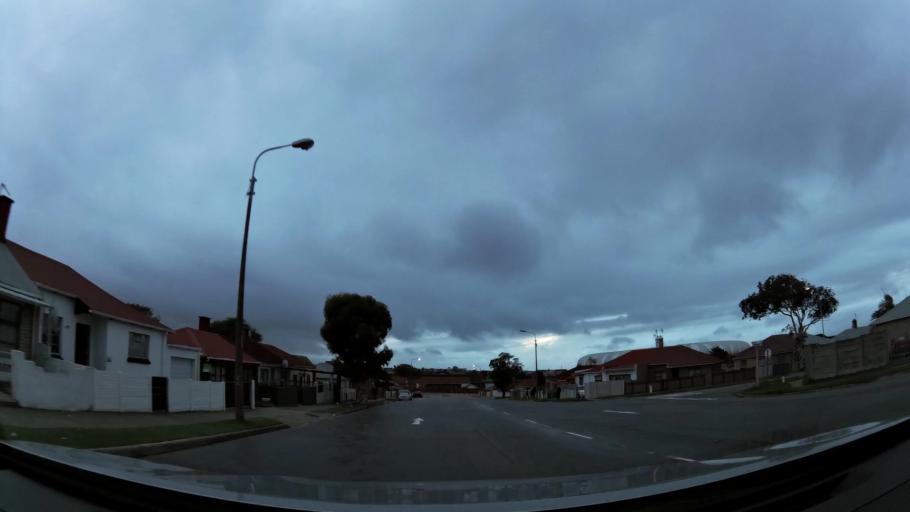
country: ZA
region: Eastern Cape
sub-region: Nelson Mandela Bay Metropolitan Municipality
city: Port Elizabeth
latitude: -33.9400
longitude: 25.5925
